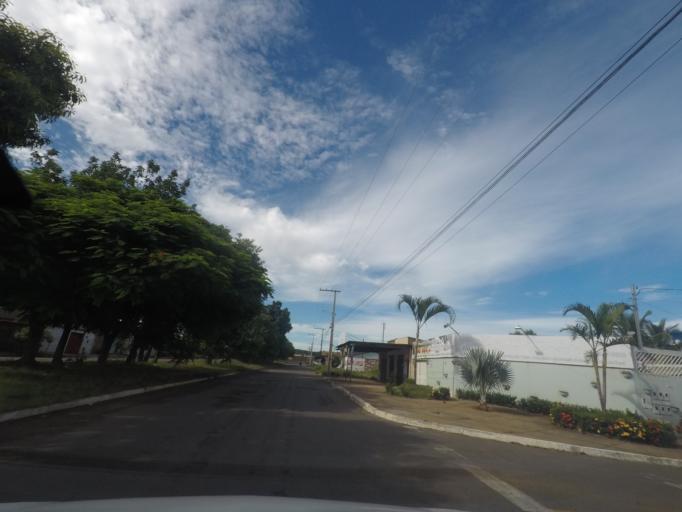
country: BR
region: Goias
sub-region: Aparecida De Goiania
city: Aparecida de Goiania
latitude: -16.8273
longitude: -49.2976
